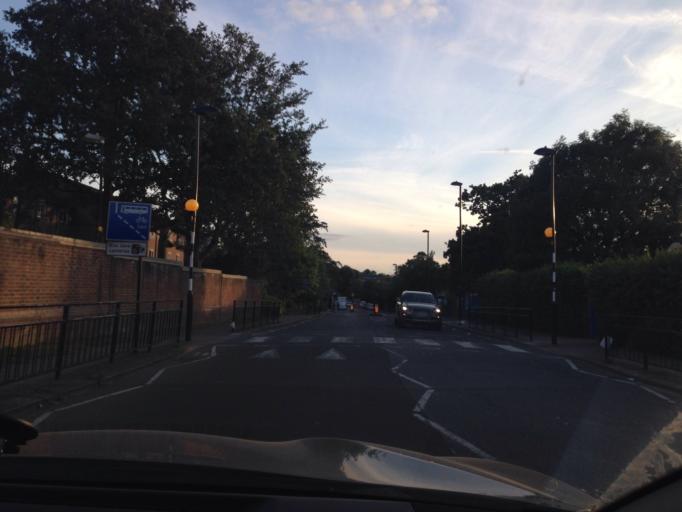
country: GB
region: England
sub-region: Greater London
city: Wembley
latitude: 51.5339
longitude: -0.2826
